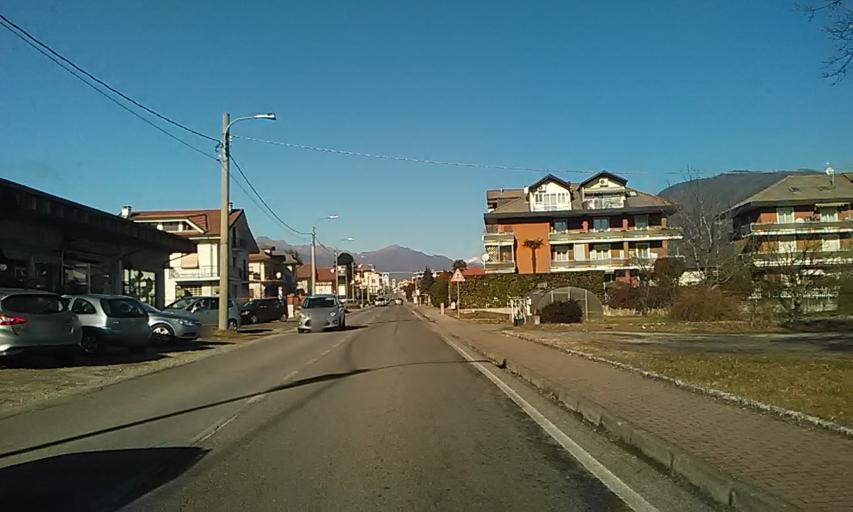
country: IT
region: Piedmont
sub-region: Provincia di Vercelli
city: Serravalle Sesia
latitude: 45.6759
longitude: 8.3208
